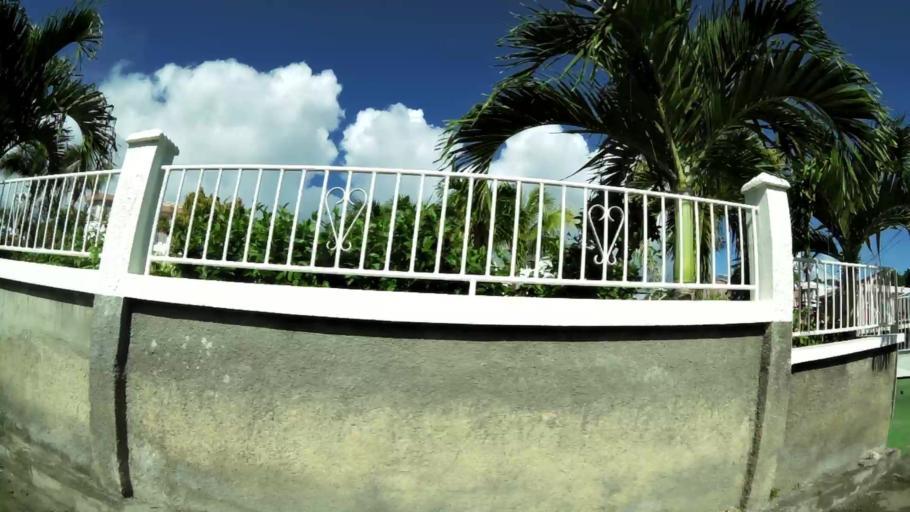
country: GP
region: Guadeloupe
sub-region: Guadeloupe
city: Sainte-Anne
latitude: 16.2342
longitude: -61.3766
